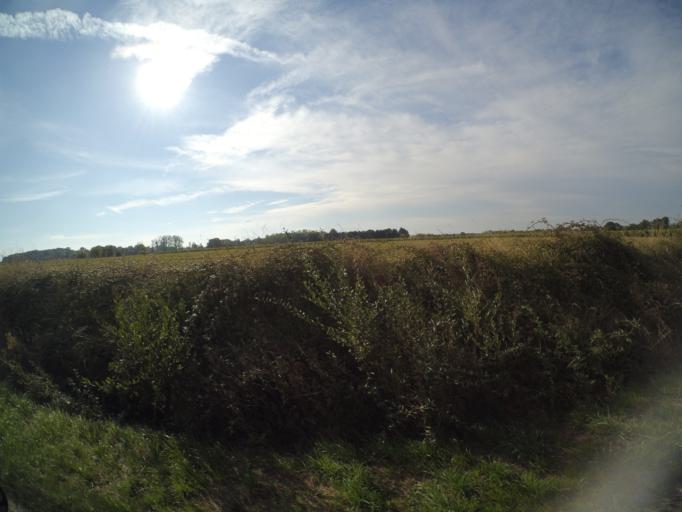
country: FR
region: Pays de la Loire
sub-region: Departement de la Loire-Atlantique
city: Mouzillon
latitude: 47.1275
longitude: -1.2613
